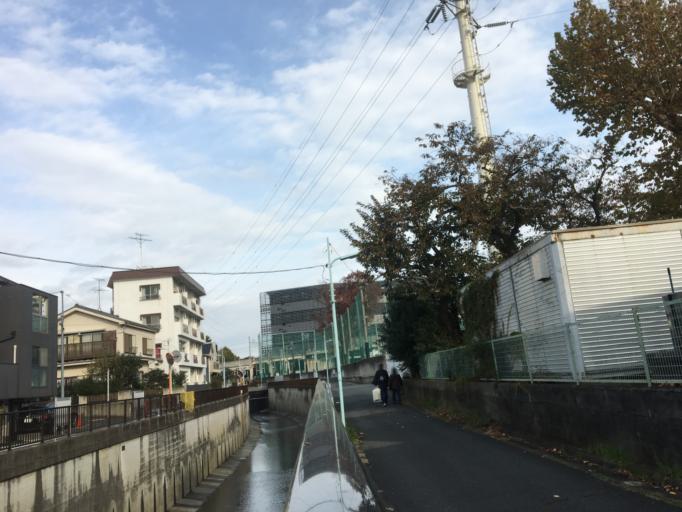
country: JP
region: Tokyo
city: Tokyo
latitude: 35.6042
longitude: 139.6807
